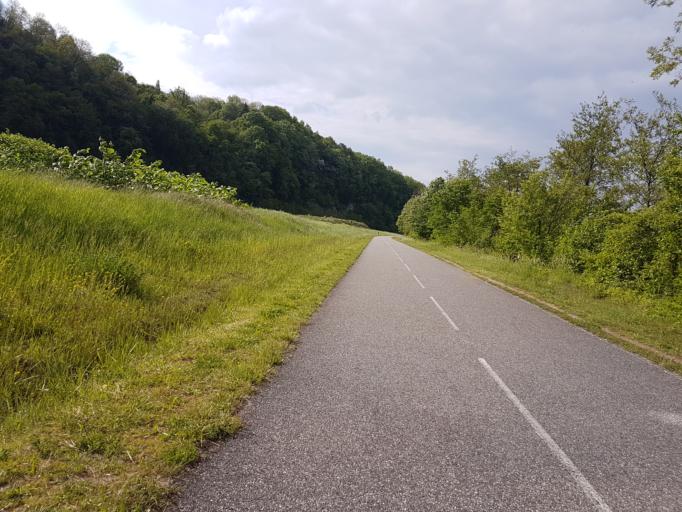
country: FR
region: Rhone-Alpes
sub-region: Departement de la Haute-Savoie
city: Versonnex
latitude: 45.9484
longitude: 5.8374
